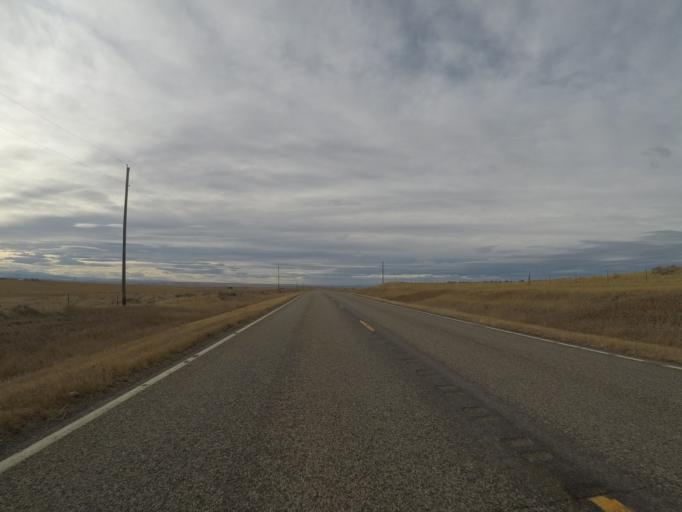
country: US
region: Montana
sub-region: Yellowstone County
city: Laurel
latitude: 45.8566
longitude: -108.8424
